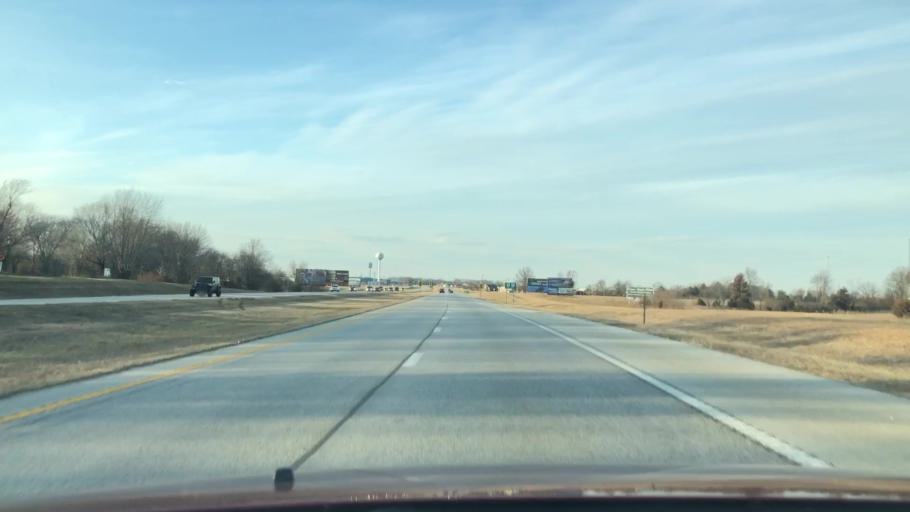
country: US
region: Missouri
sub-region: Webster County
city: Seymour
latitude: 37.1457
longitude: -92.7488
